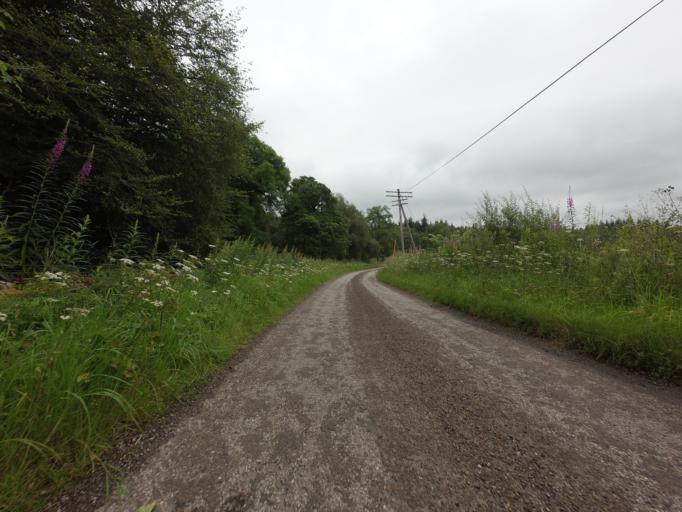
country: GB
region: Scotland
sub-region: Highland
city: Evanton
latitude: 57.9831
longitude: -4.4189
